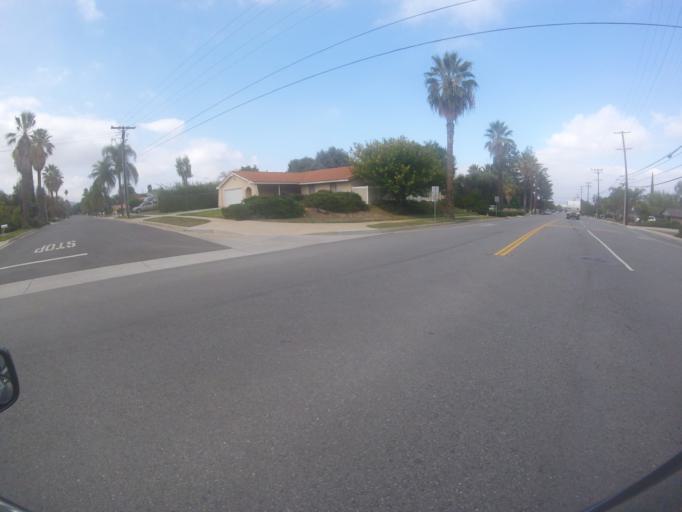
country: US
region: California
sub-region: San Bernardino County
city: Redlands
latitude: 34.0378
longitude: -117.1897
